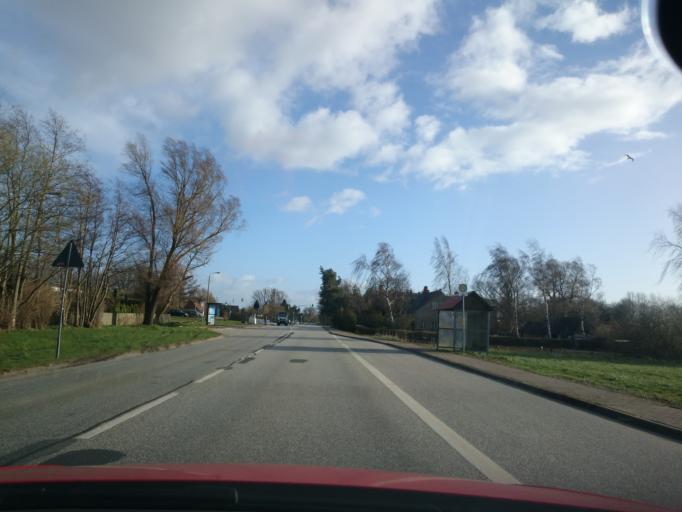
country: DE
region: Mecklenburg-Vorpommern
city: Barth
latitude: 54.2968
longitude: 12.7190
